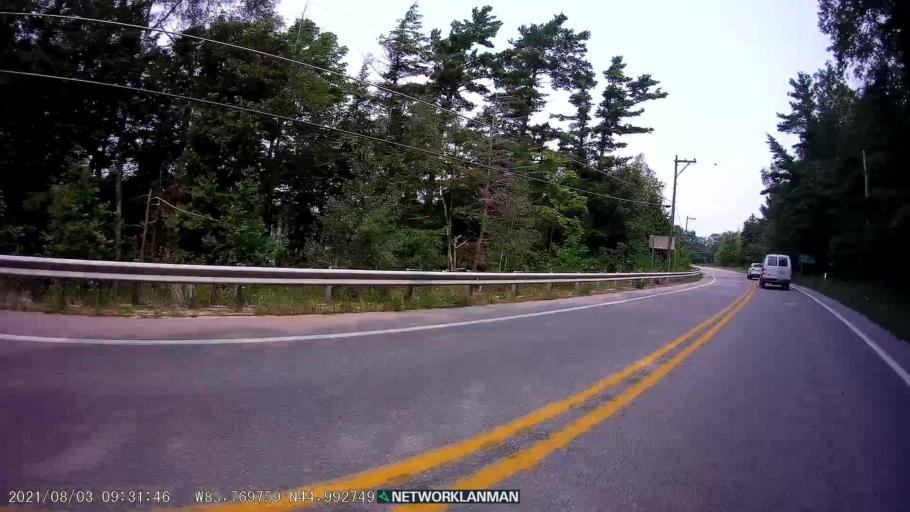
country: US
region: Michigan
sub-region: Leelanau County
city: Leland
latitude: 44.9923
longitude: -85.7701
